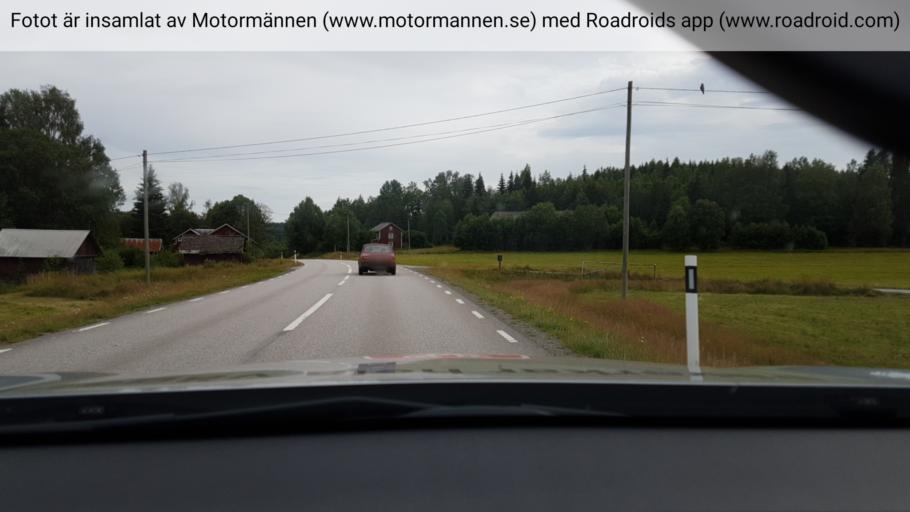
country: SE
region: Vaestra Goetaland
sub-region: Bengtsfors Kommun
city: Dals Langed
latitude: 58.8891
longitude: 12.2106
